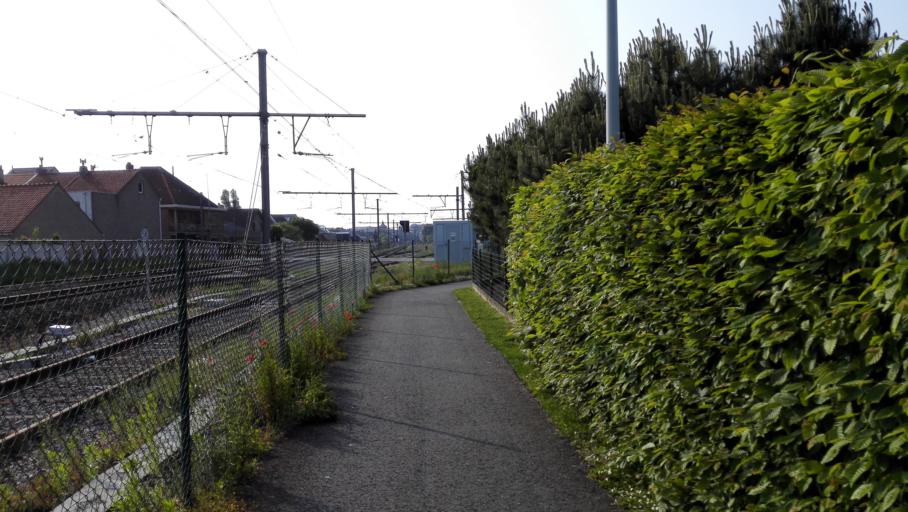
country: BE
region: Flanders
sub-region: Provincie West-Vlaanderen
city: Blankenberge
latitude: 51.3057
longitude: 3.1439
